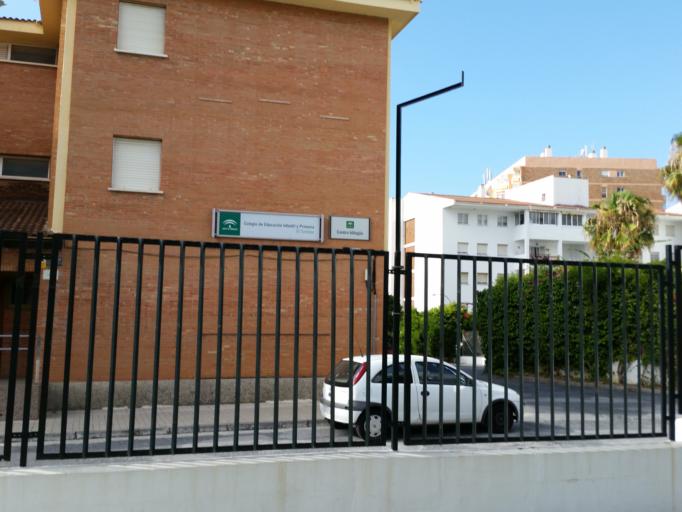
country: ES
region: Andalusia
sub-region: Provincia de Malaga
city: Torremolinos
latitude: 36.6008
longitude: -4.5276
